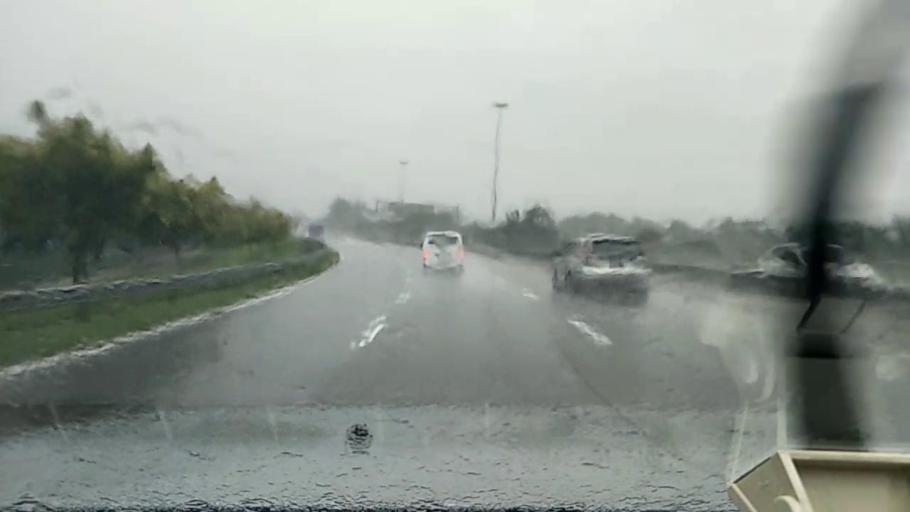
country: MY
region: Selangor
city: Kampong Baharu Balakong
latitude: 3.0001
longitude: 101.7751
